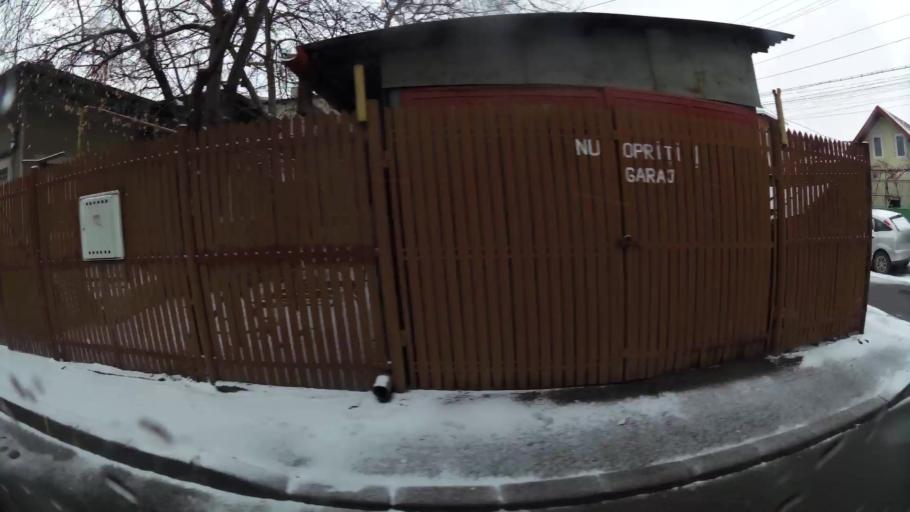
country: RO
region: Prahova
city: Ploiesti
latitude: 44.9282
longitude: 26.0203
